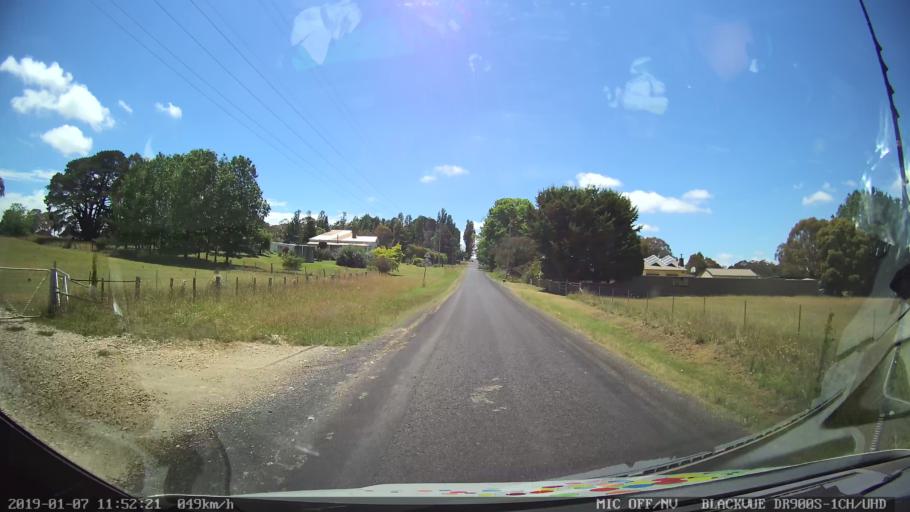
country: AU
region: New South Wales
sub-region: Guyra
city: Guyra
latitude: -30.3085
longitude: 151.6541
